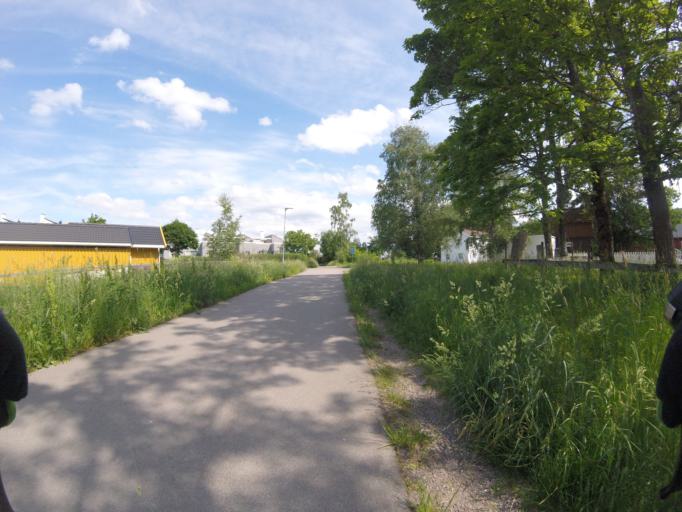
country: NO
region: Akershus
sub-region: Skedsmo
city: Lillestrom
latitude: 59.9847
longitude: 11.0350
